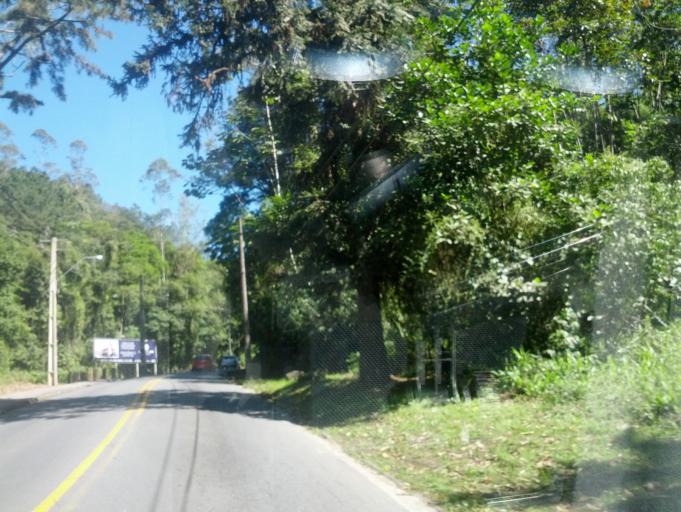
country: BR
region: Santa Catarina
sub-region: Blumenau
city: Blumenau
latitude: -26.9234
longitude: -49.0828
